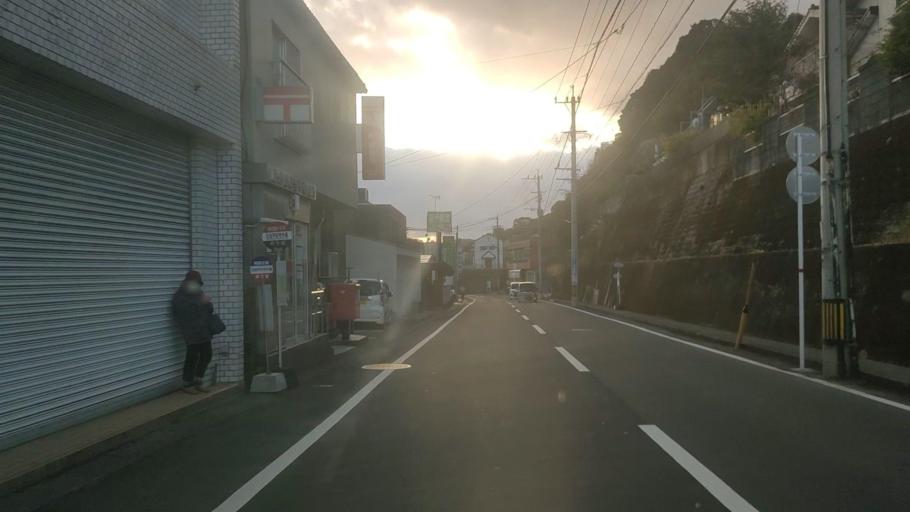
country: JP
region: Kagoshima
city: Kagoshima-shi
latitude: 31.6209
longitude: 130.5383
